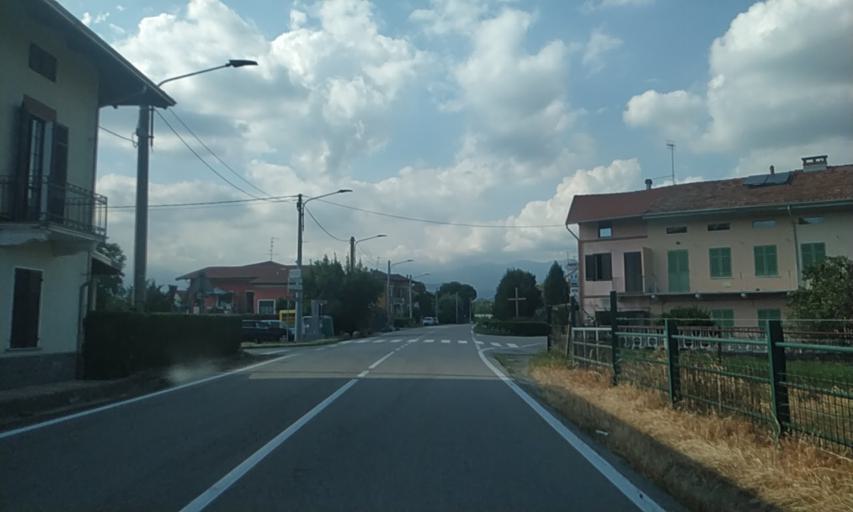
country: IT
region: Piedmont
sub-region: Provincia di Biella
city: Cerreto Castello
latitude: 45.5483
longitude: 8.1759
